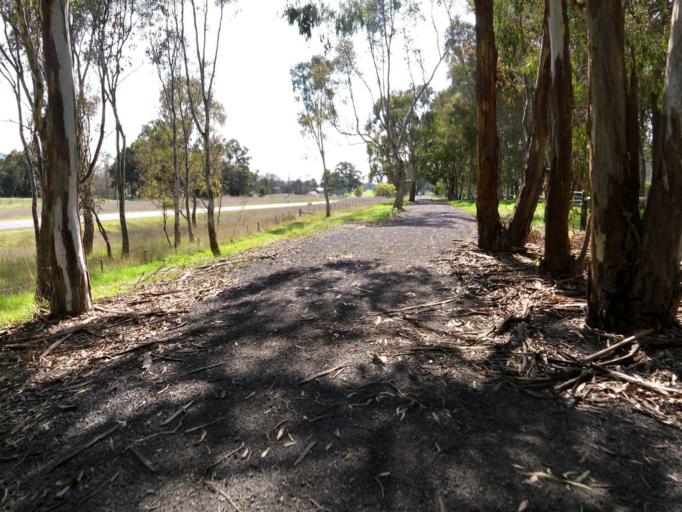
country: AU
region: Victoria
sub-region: Murrindindi
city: Alexandra
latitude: -37.1311
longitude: 145.5942
